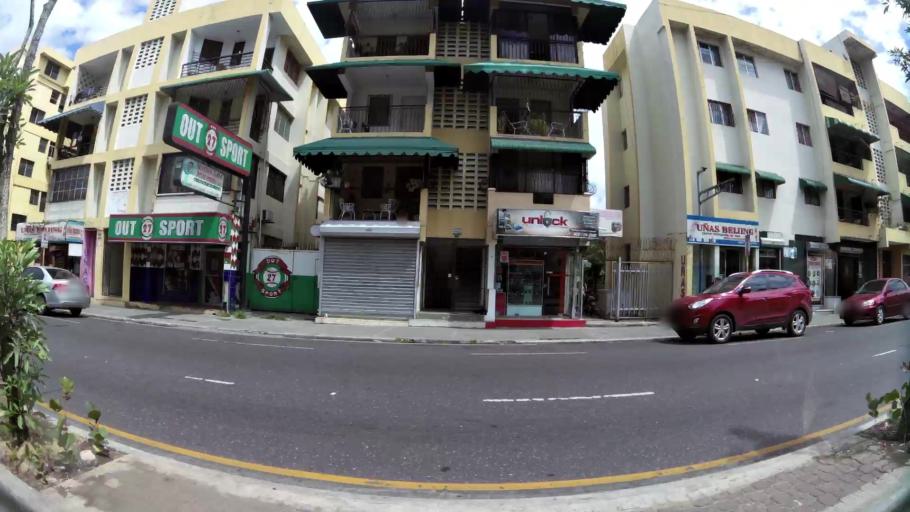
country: DO
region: Santiago
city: Santiago de los Caballeros
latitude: 19.4544
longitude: -70.7019
